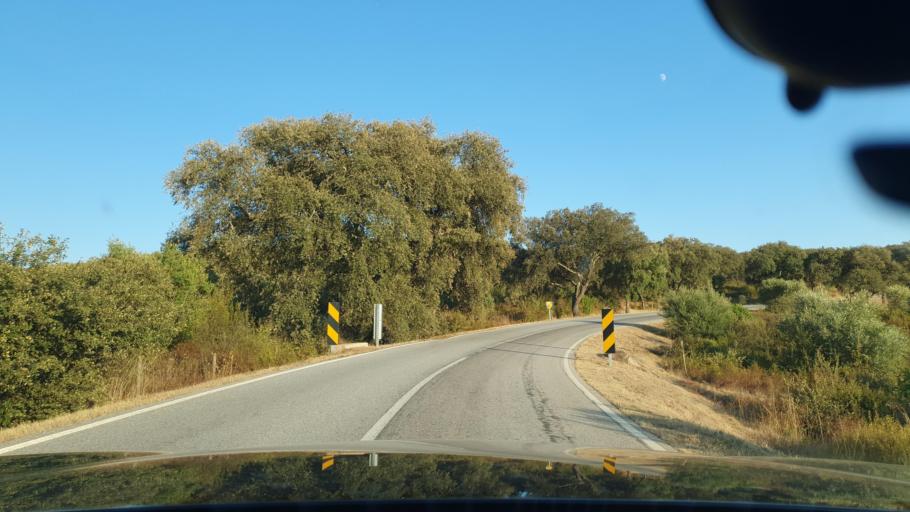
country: PT
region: Evora
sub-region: Estremoz
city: Estremoz
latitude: 38.9141
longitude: -7.6632
